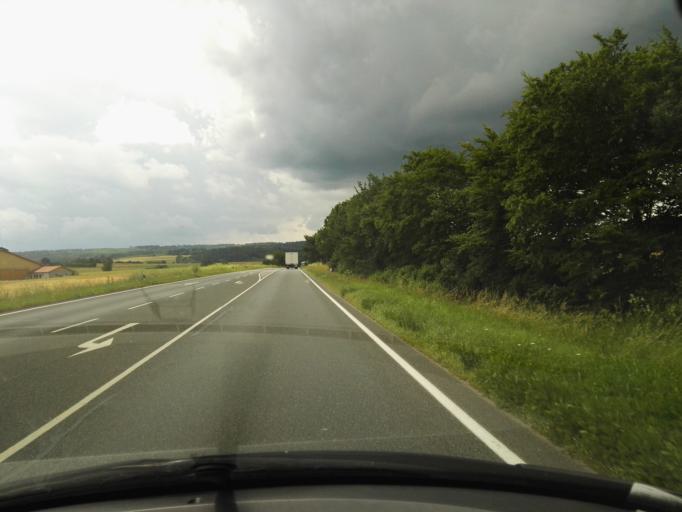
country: DE
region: Bavaria
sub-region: Upper Franconia
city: Hochstadt am Main
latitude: 50.1488
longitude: 11.1637
